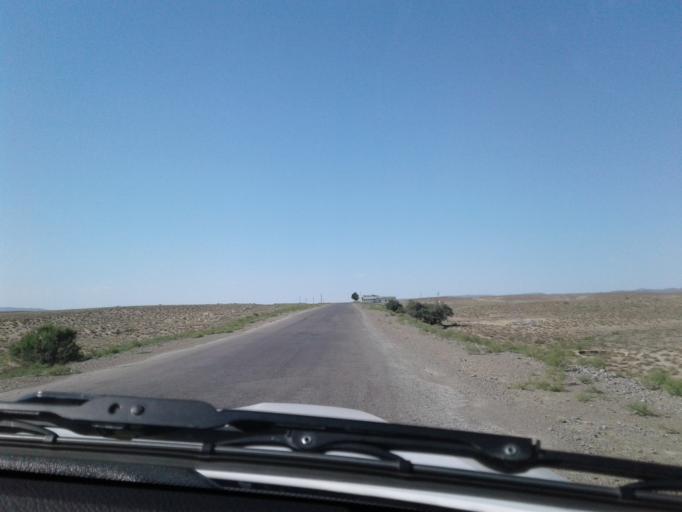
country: TM
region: Balkan
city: Serdar
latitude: 38.7176
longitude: 56.2925
